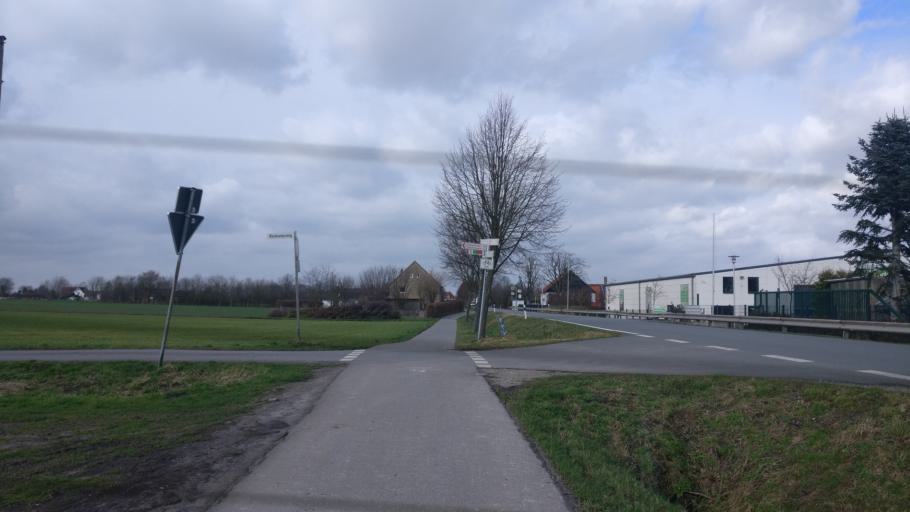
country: DE
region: North Rhine-Westphalia
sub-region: Regierungsbezirk Detmold
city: Lage
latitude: 52.0219
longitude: 8.7832
